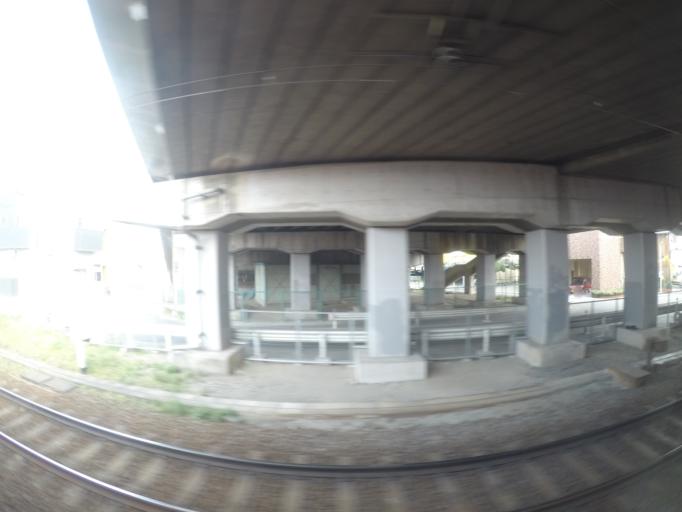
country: JP
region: Aichi
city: Nagoya-shi
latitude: 35.0907
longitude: 136.9122
